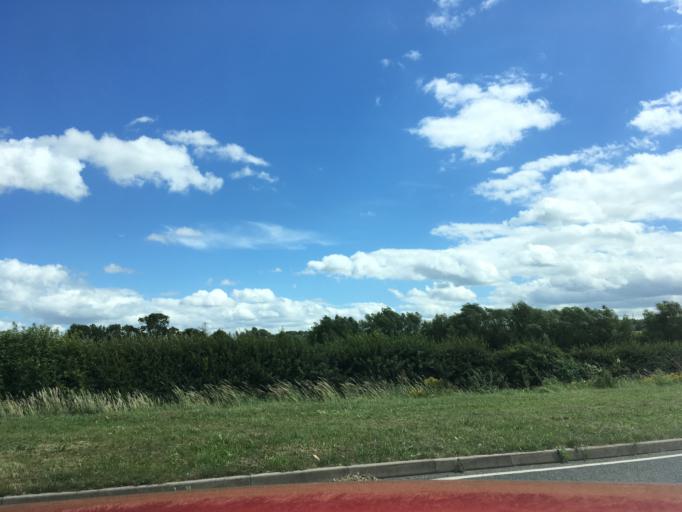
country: GB
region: England
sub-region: Nottinghamshire
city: Cotgrave
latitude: 52.9173
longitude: -1.0289
